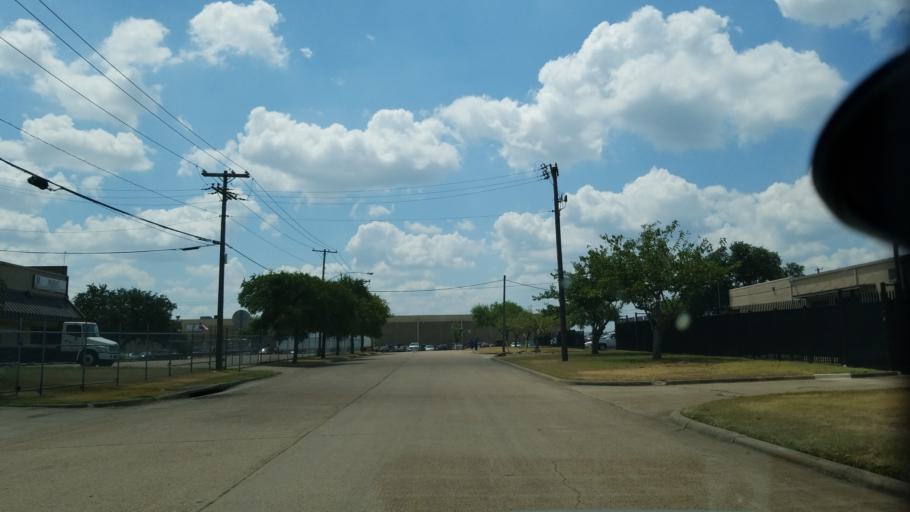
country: US
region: Texas
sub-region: Dallas County
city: Duncanville
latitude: 32.6835
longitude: -96.8864
